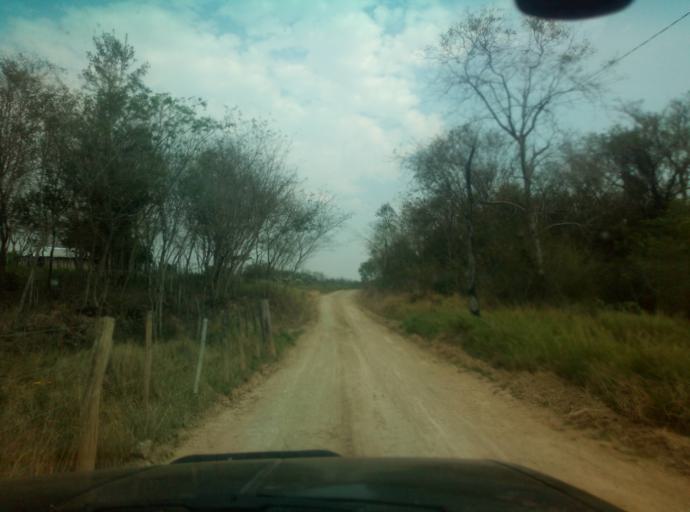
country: PY
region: Caaguazu
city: San Joaquin
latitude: -25.0952
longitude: -56.1403
